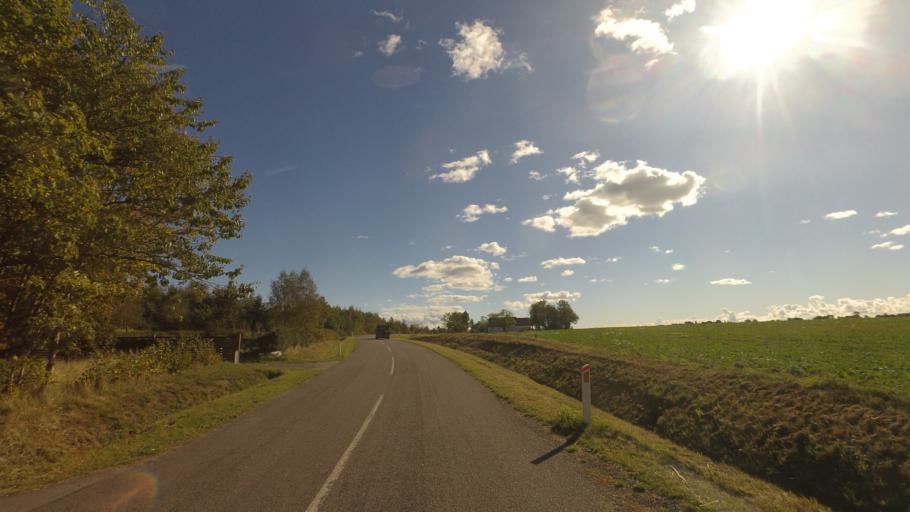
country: DK
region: Capital Region
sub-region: Bornholm Kommune
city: Akirkeby
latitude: 55.1315
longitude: 15.0230
